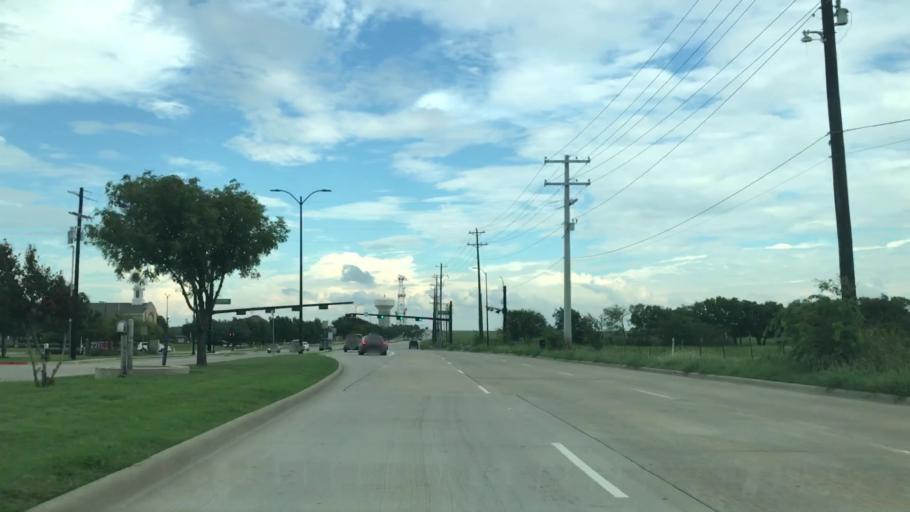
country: US
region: Texas
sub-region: Collin County
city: Frisco
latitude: 33.1745
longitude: -96.7871
